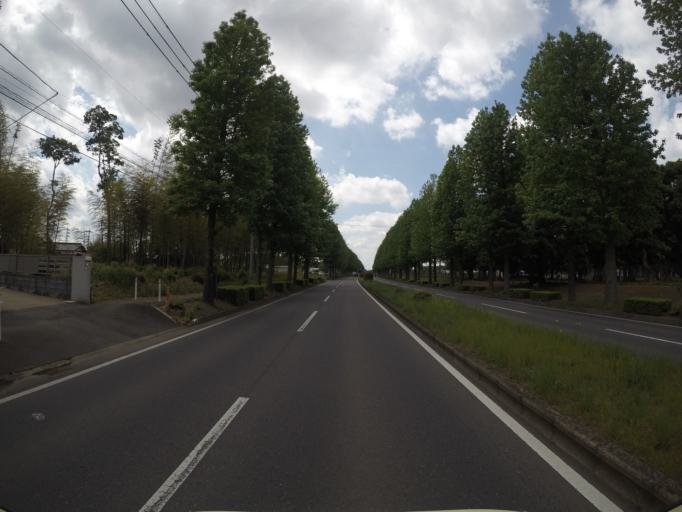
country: JP
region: Ibaraki
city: Naka
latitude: 36.0472
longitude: 140.1020
